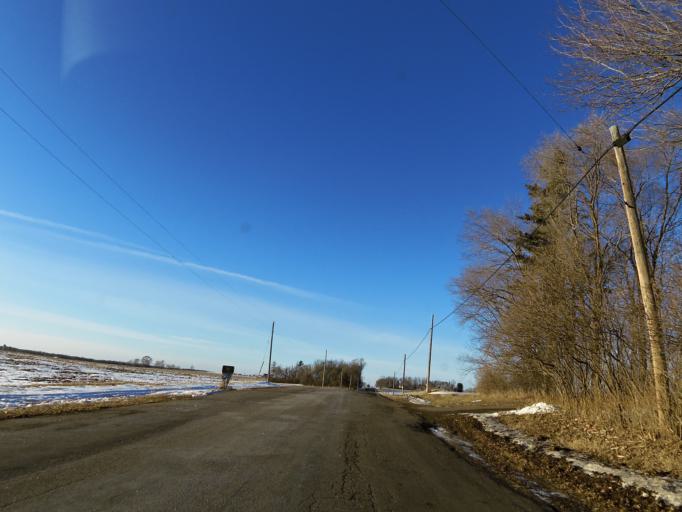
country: US
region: Minnesota
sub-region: Dakota County
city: Hastings
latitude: 44.8050
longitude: -92.8746
